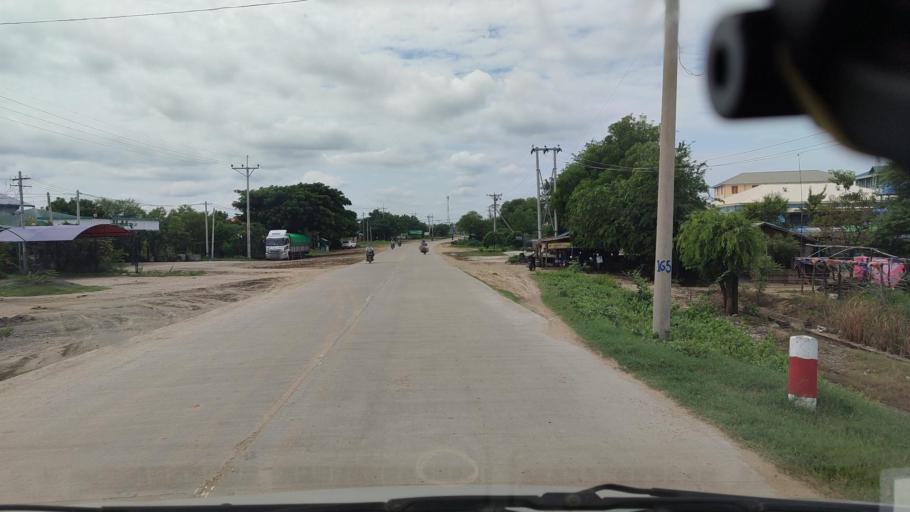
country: MM
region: Mandalay
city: Yamethin
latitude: 20.5874
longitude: 96.0431
